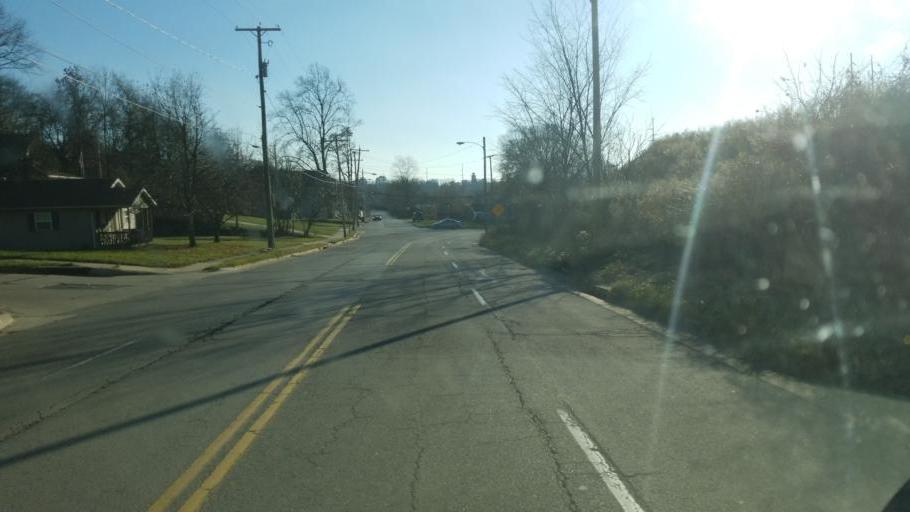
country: US
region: Ohio
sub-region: Summit County
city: Akron
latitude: 41.0811
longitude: -81.4820
